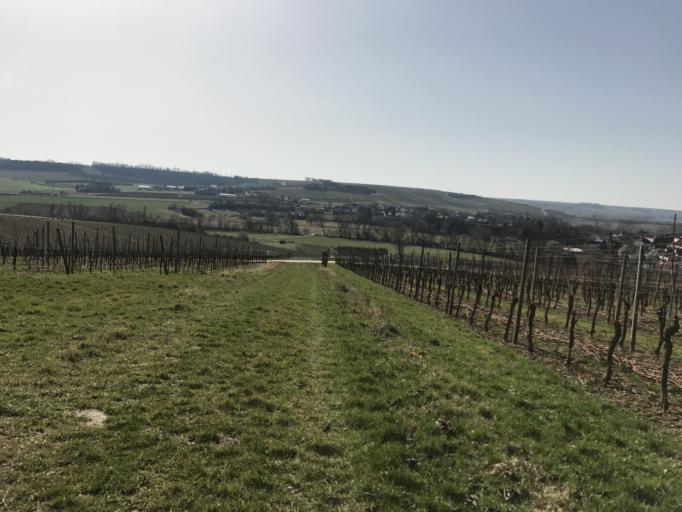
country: DE
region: Rheinland-Pfalz
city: Essenheim
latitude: 49.9173
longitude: 8.1431
